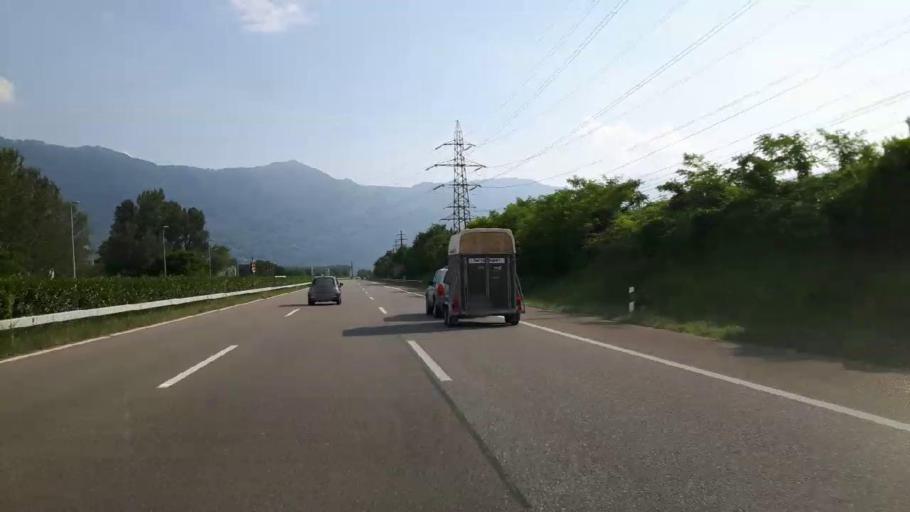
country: CH
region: Ticino
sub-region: Bellinzona District
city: Monte Carasso
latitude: 46.1883
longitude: 9.0051
